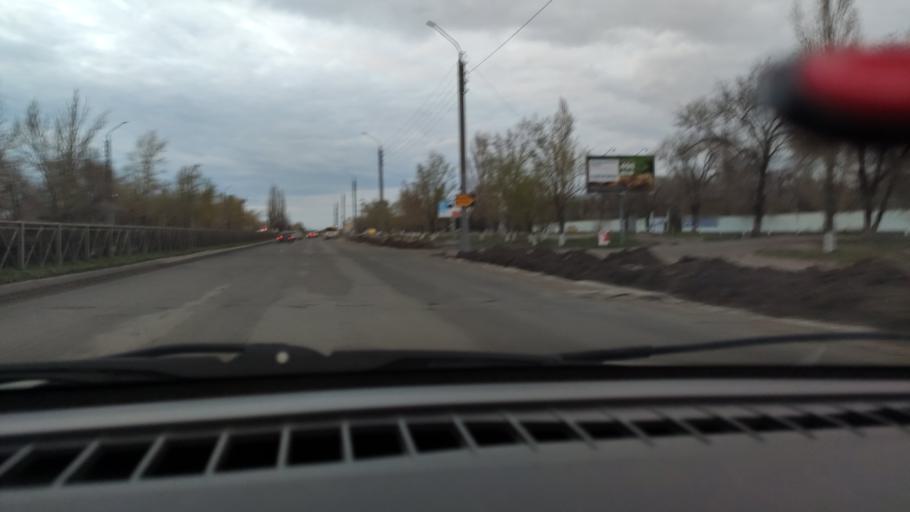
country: RU
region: Orenburg
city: Orenburg
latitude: 51.8199
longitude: 55.1077
